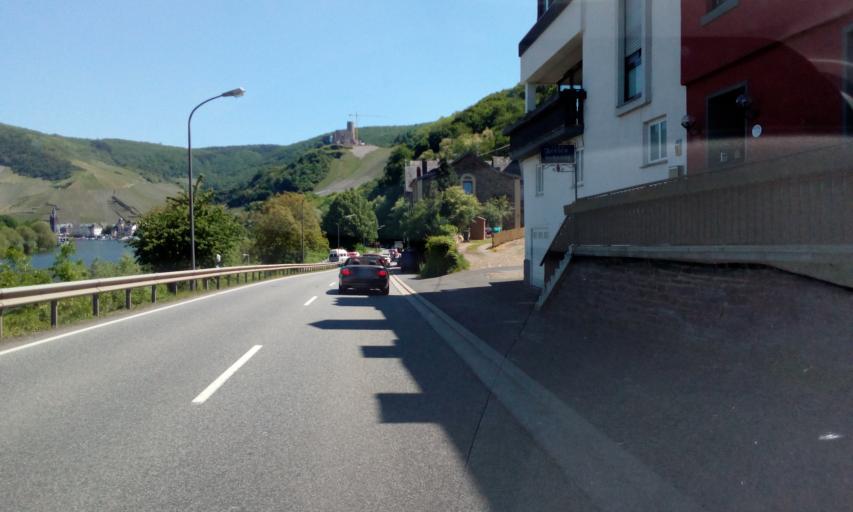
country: DE
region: Rheinland-Pfalz
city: Monzelfeld
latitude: 49.9076
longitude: 7.0622
